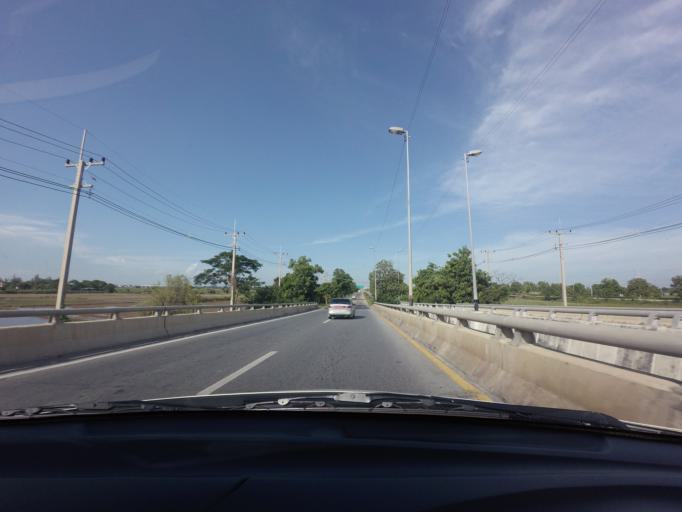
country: TH
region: Suphan Buri
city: Suphan Buri
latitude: 14.4459
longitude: 100.1329
